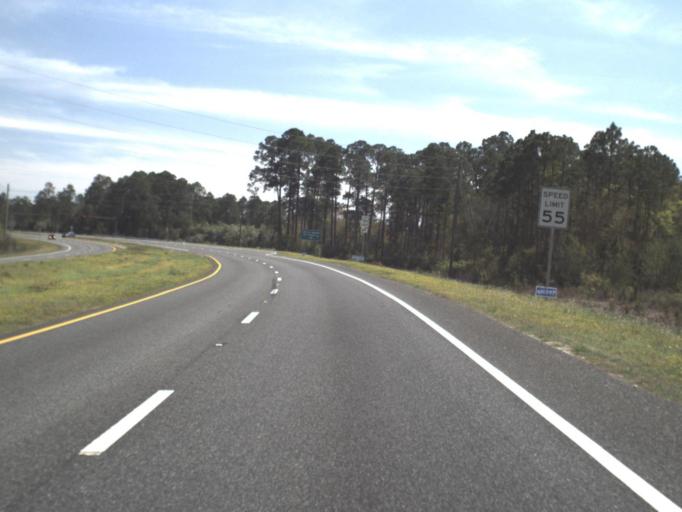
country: US
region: Florida
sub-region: Bay County
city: Lynn Haven
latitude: 30.3249
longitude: -85.6608
